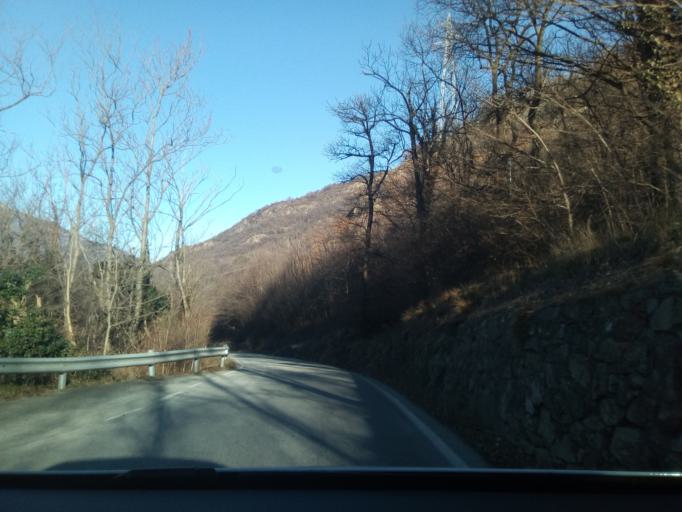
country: IT
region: Piedmont
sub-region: Provincia di Torino
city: Andrate
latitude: 45.5116
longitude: 7.8770
